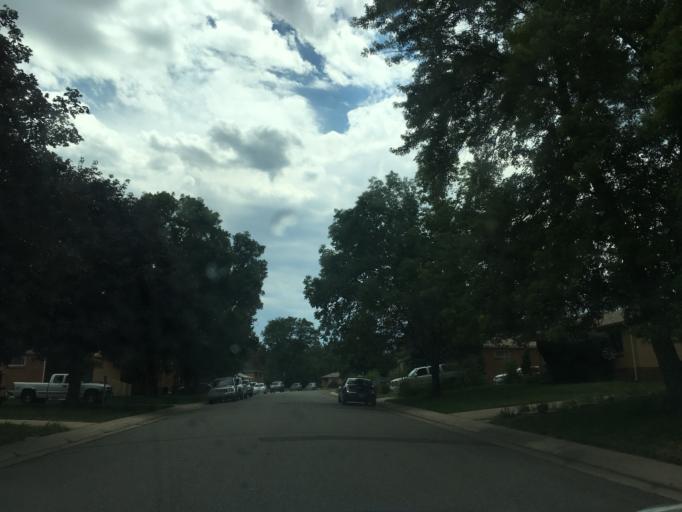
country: US
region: Colorado
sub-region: Arapahoe County
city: Sheridan
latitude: 39.6726
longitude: -105.0473
